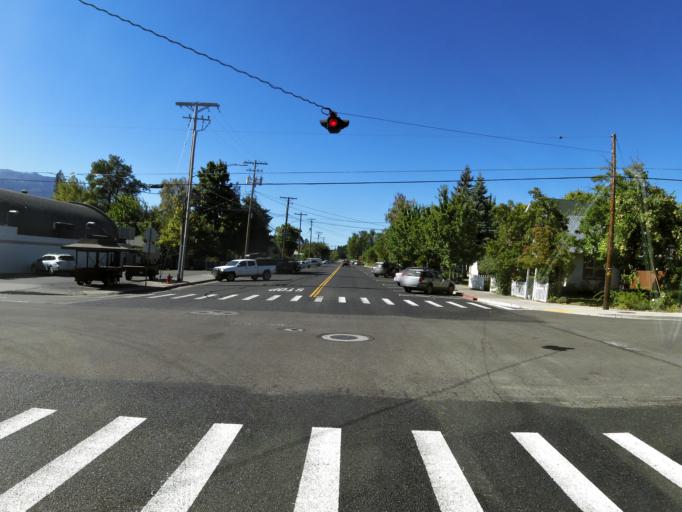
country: US
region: California
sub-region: Siskiyou County
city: Mount Shasta
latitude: 41.3156
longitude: -122.3138
